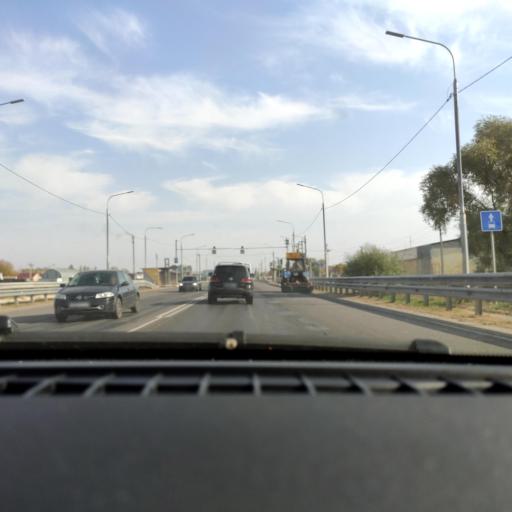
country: RU
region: Voronezj
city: Somovo
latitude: 51.6904
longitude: 39.3647
